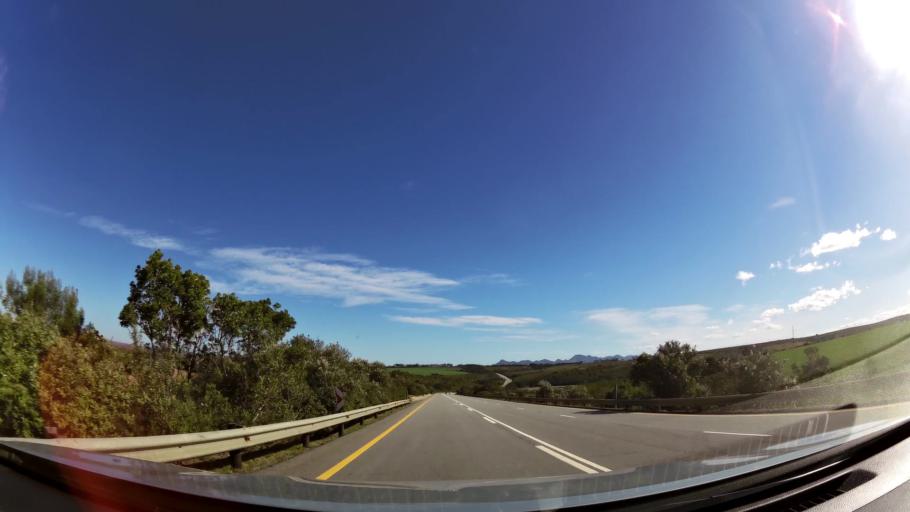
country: ZA
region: Eastern Cape
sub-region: Cacadu District Municipality
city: Kruisfontein
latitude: -34.0123
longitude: 24.6449
